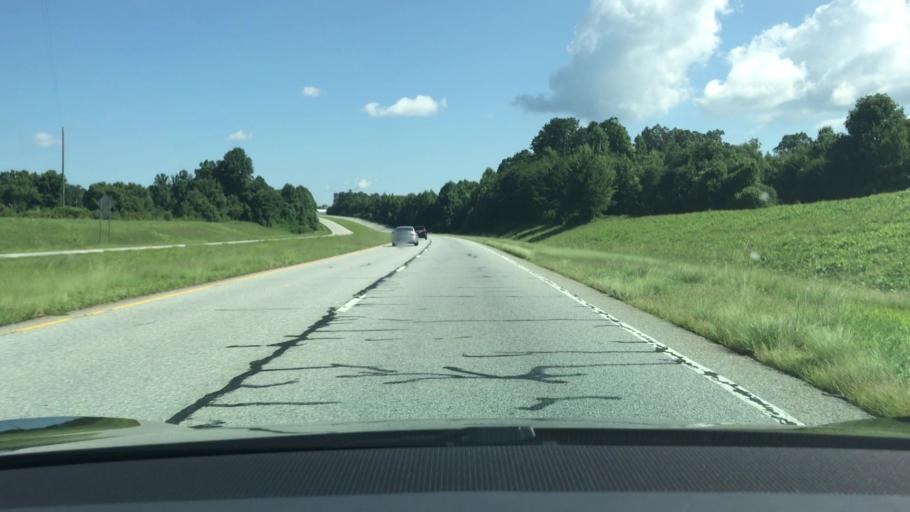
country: US
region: Georgia
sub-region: Habersham County
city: Clarkesville
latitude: 34.6182
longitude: -83.4476
